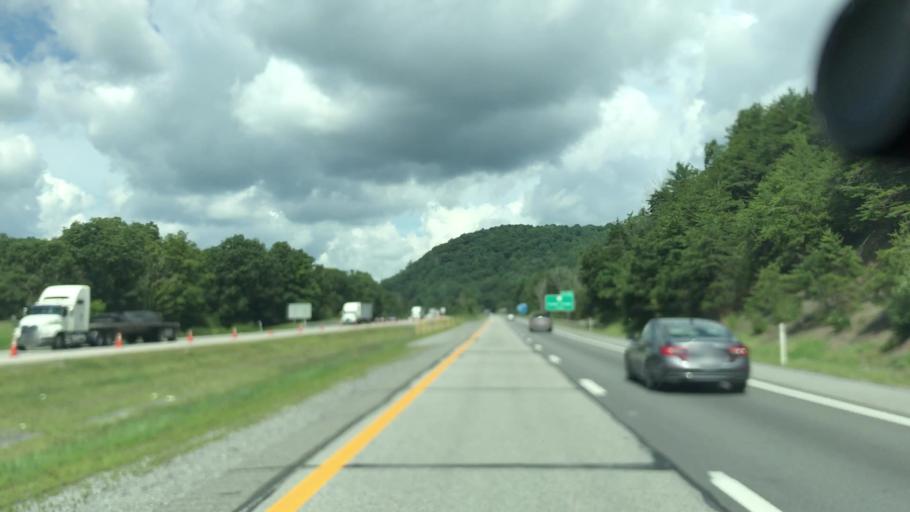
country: US
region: West Virginia
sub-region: Mercer County
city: Athens
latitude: 37.4895
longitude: -81.0850
